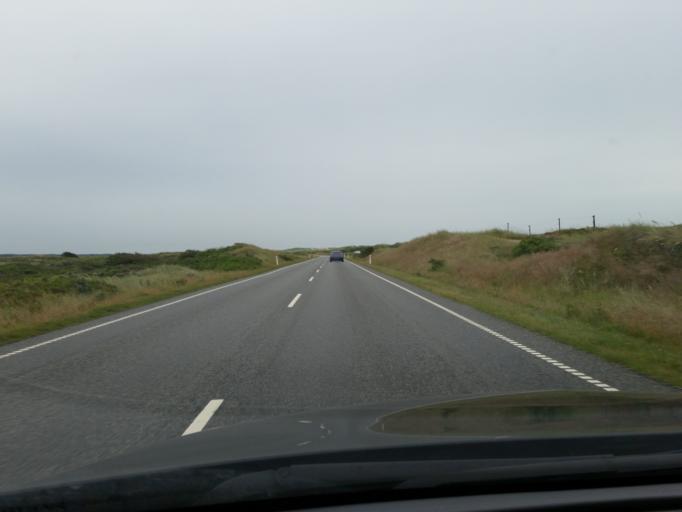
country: DK
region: Central Jutland
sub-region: Ringkobing-Skjern Kommune
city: Hvide Sande
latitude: 55.8305
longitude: 8.1727
